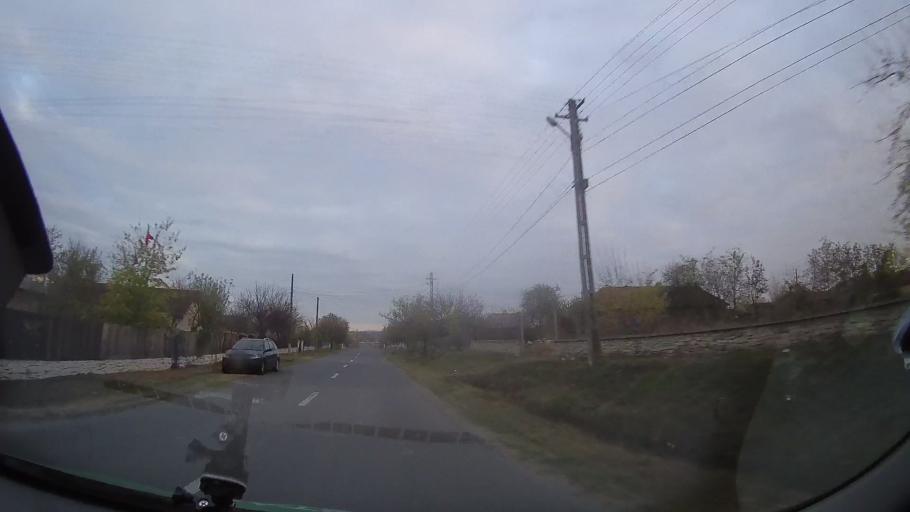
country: RO
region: Tulcea
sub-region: Comuna Mihai Bravu
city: Turda
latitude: 44.9755
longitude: 28.6217
